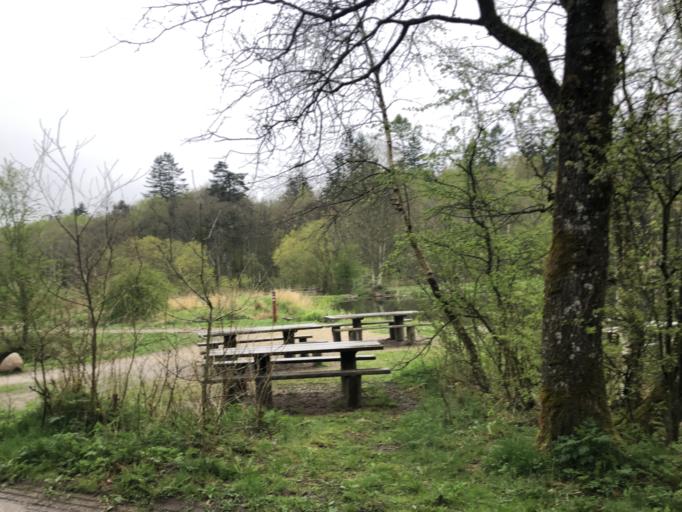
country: DK
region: Central Jutland
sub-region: Lemvig Kommune
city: Lemvig
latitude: 56.4850
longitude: 8.3632
